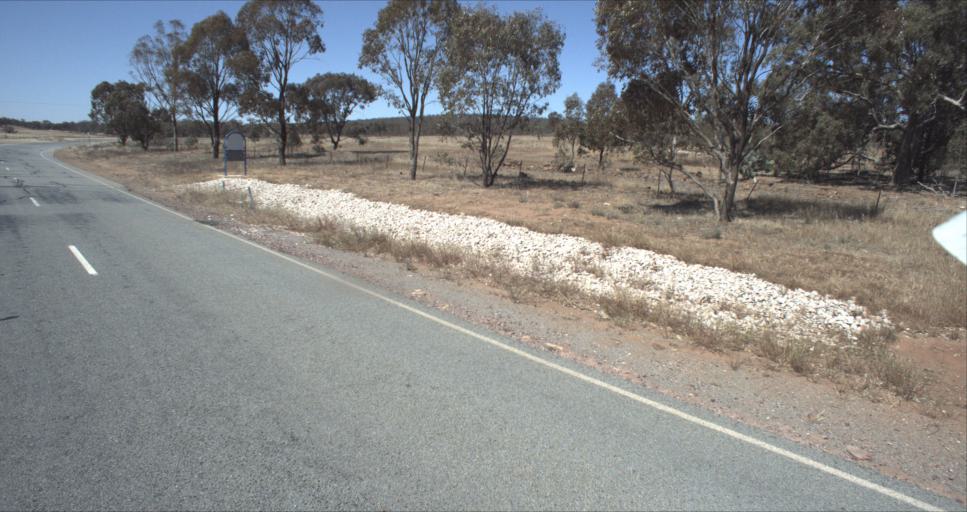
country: AU
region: New South Wales
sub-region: Leeton
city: Leeton
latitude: -34.4805
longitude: 146.4778
